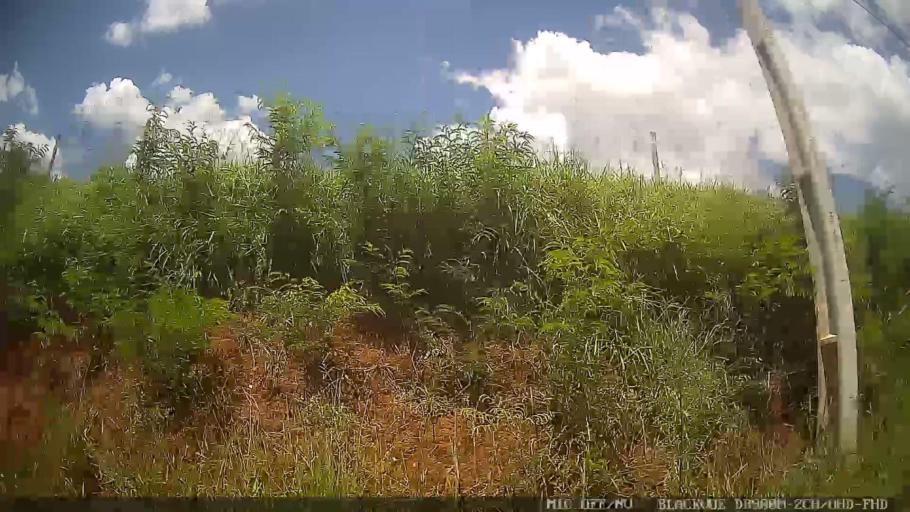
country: BR
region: Minas Gerais
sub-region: Extrema
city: Extrema
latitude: -22.8495
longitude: -46.2770
